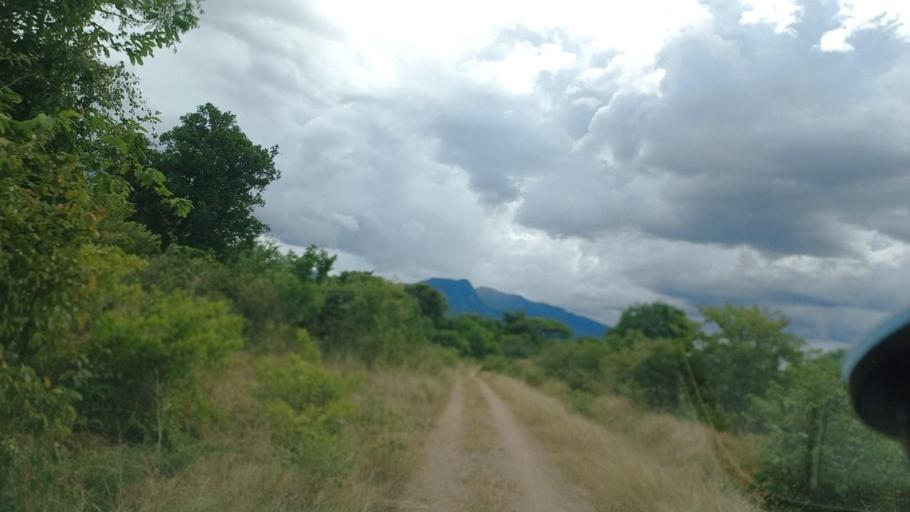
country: ZM
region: Lusaka
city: Luangwa
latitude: -15.6522
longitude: 30.3508
